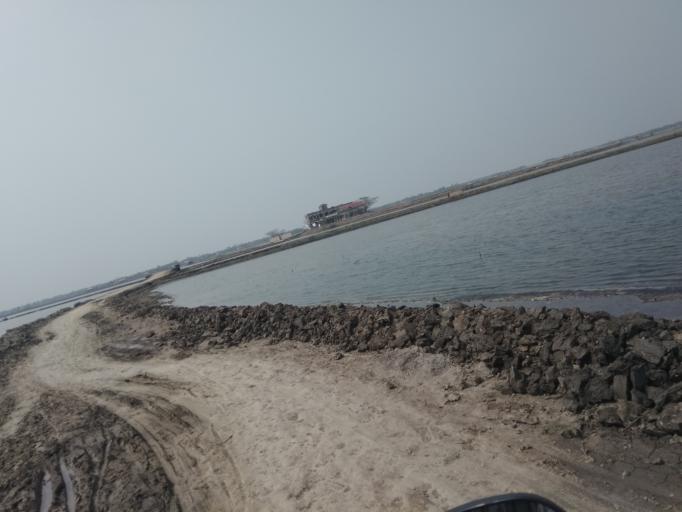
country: IN
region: West Bengal
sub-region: North 24 Parganas
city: Taki
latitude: 22.3443
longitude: 89.2308
